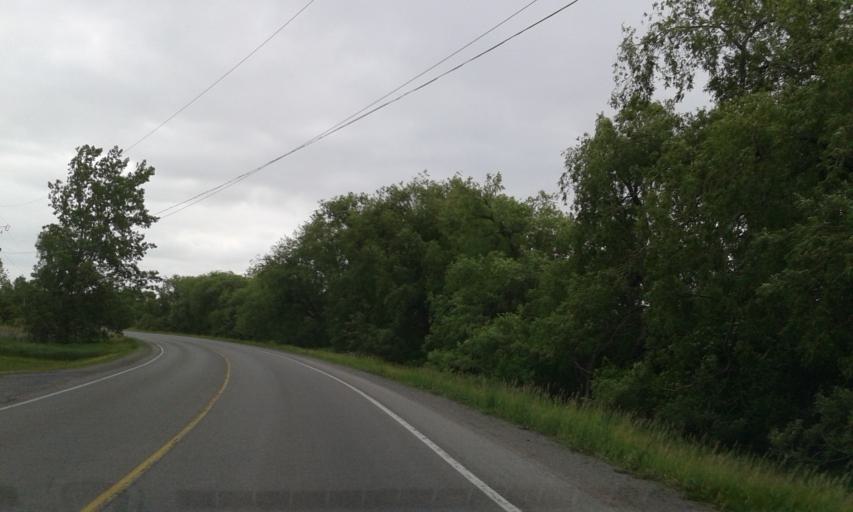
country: CA
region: Ontario
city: Prince Edward
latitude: 43.9614
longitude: -77.2935
